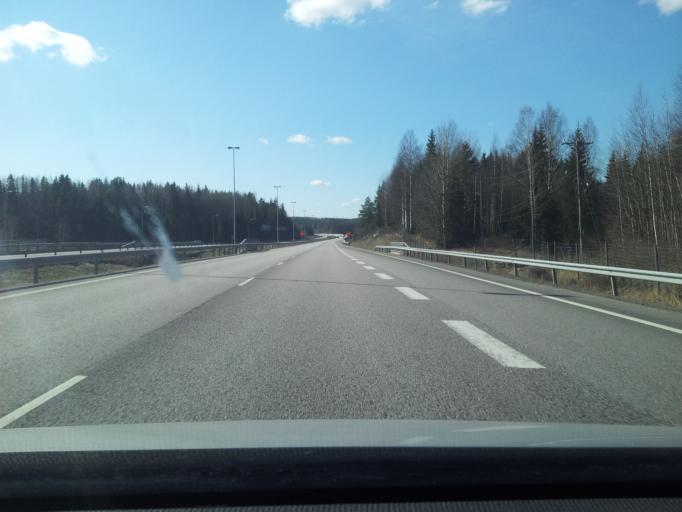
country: FI
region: Uusimaa
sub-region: Loviisa
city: Perna
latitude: 60.4918
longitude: 25.9515
